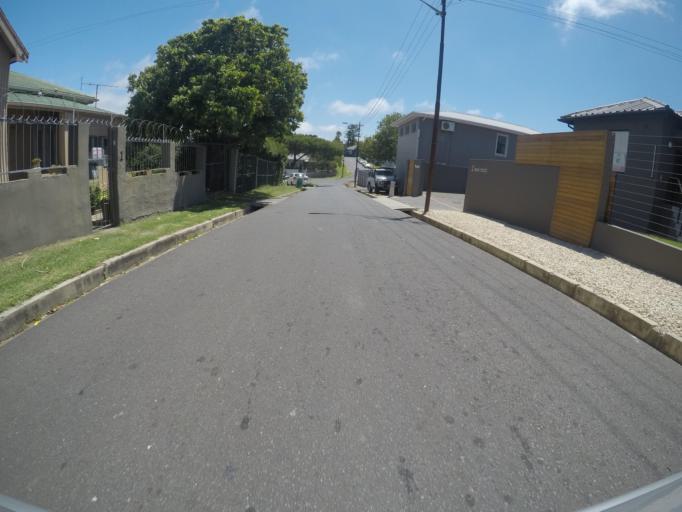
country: ZA
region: Eastern Cape
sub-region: Buffalo City Metropolitan Municipality
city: East London
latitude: -32.9861
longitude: 27.9027
